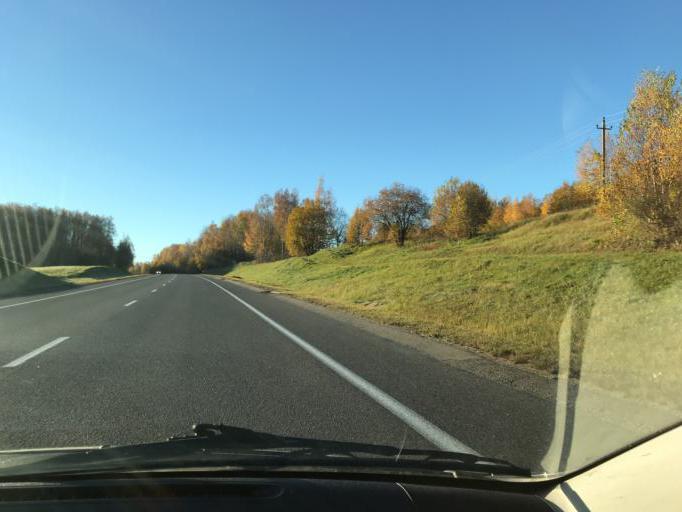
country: BY
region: Vitebsk
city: Vitebsk
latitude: 55.0485
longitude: 30.3132
